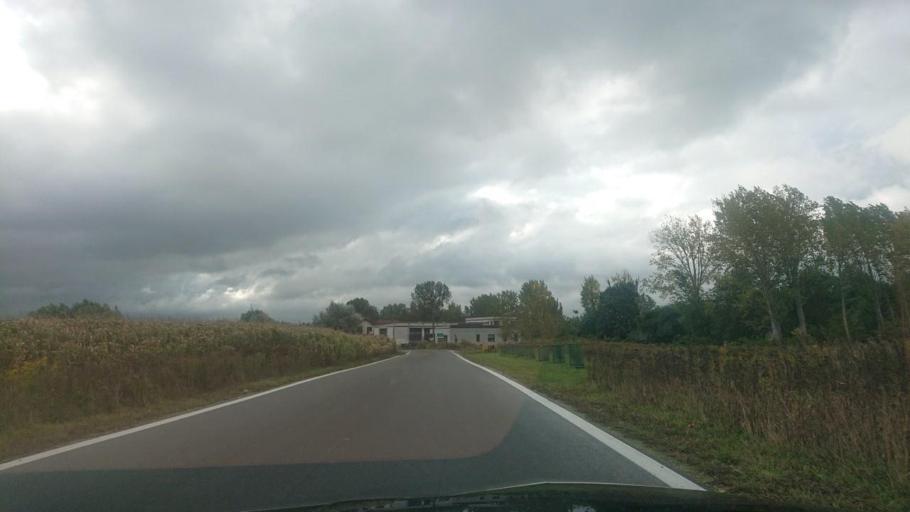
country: PL
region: Greater Poland Voivodeship
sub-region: Powiat gnieznienski
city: Gniezno
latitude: 52.5238
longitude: 17.6337
